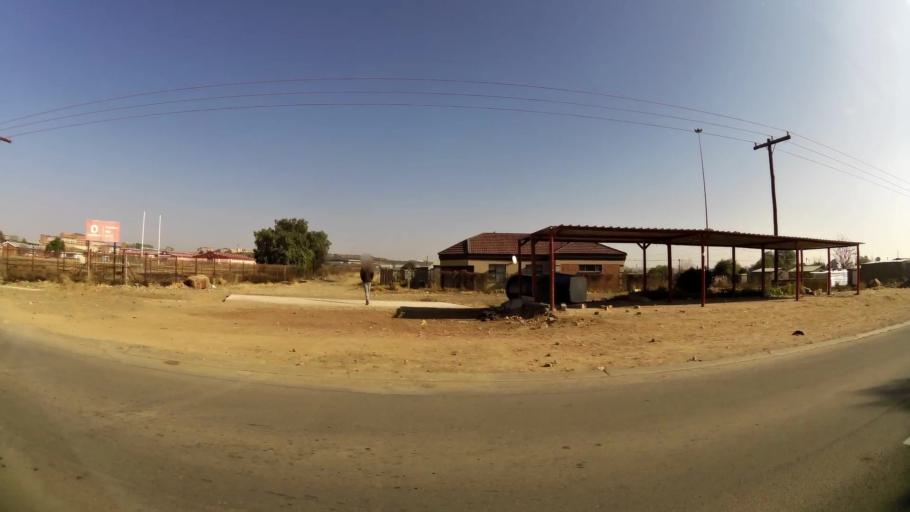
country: ZA
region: Orange Free State
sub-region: Mangaung Metropolitan Municipality
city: Bloemfontein
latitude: -29.1831
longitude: 26.2233
